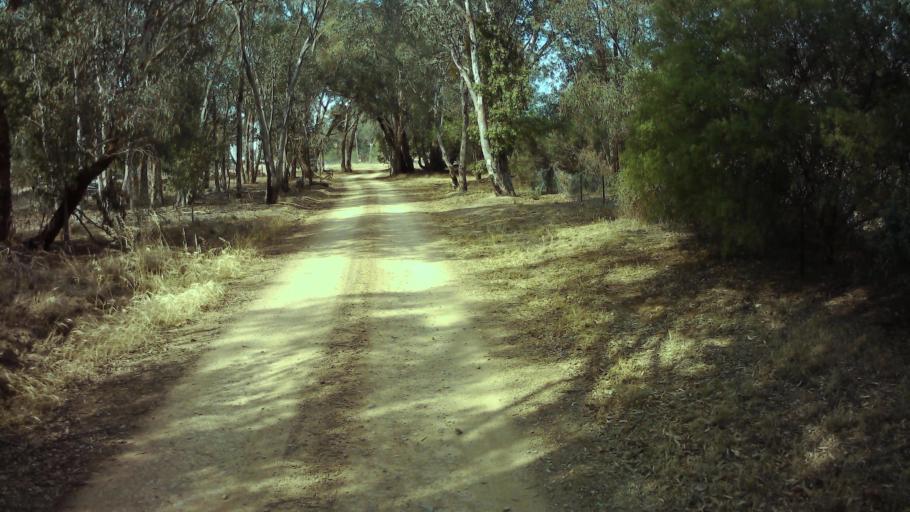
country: AU
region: New South Wales
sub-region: Weddin
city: Grenfell
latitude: -33.8982
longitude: 148.1511
